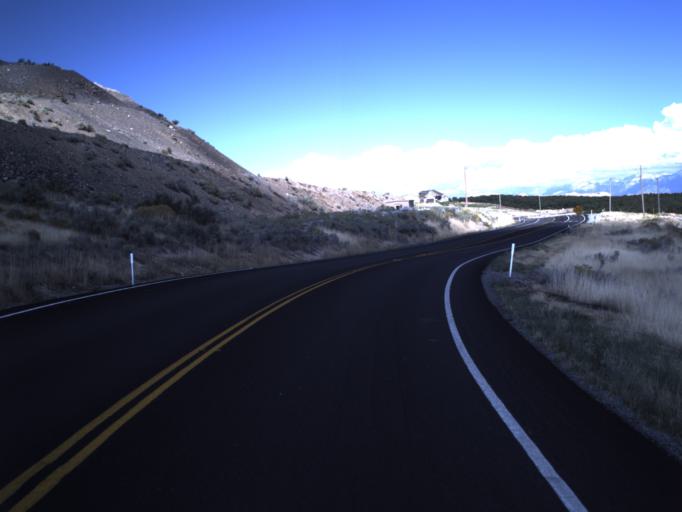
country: US
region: Utah
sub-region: Utah County
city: Santaquin
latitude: 40.0096
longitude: -111.8023
